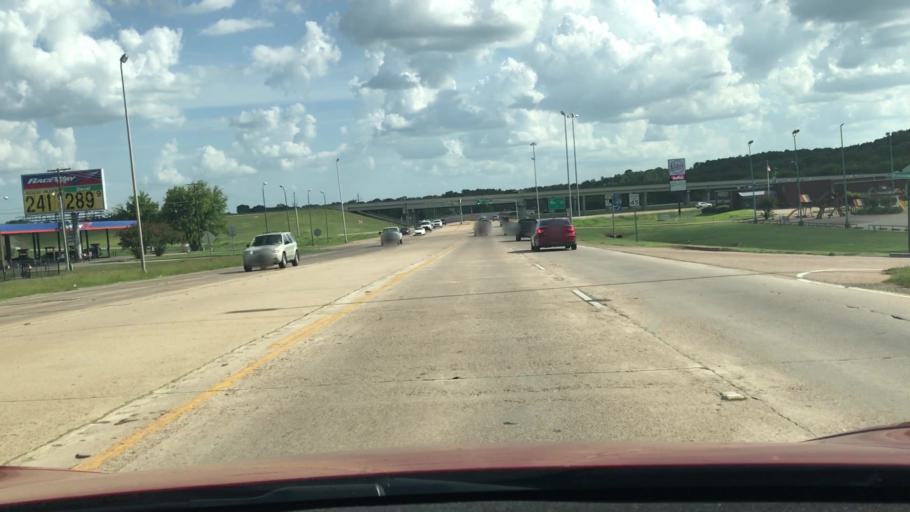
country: US
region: Louisiana
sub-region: Bossier Parish
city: Bossier City
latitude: 32.4142
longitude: -93.7238
